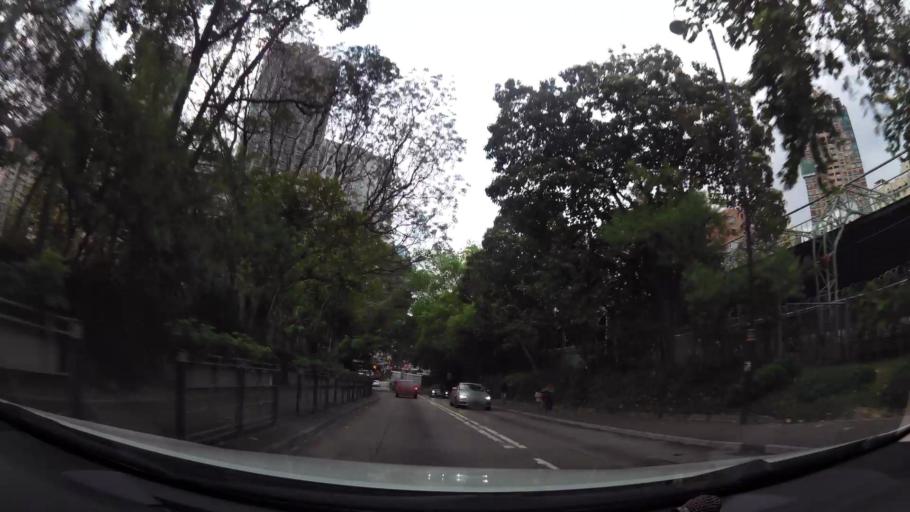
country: HK
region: Kowloon City
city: Kowloon
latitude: 22.3157
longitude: 114.1745
